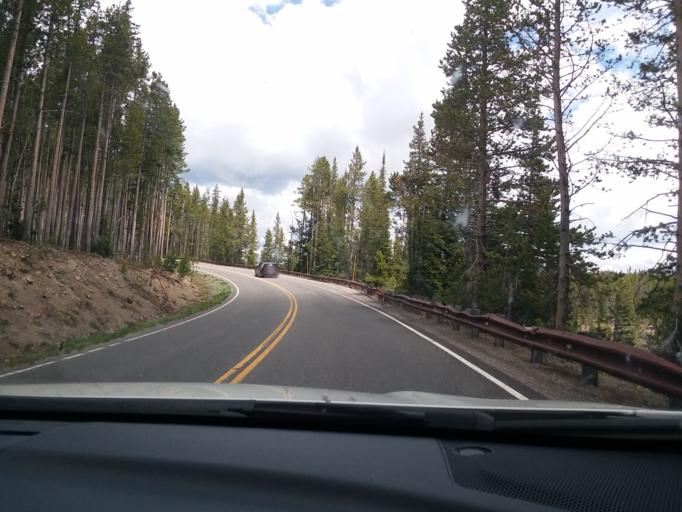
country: US
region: Montana
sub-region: Gallatin County
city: West Yellowstone
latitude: 44.1899
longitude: -110.6561
